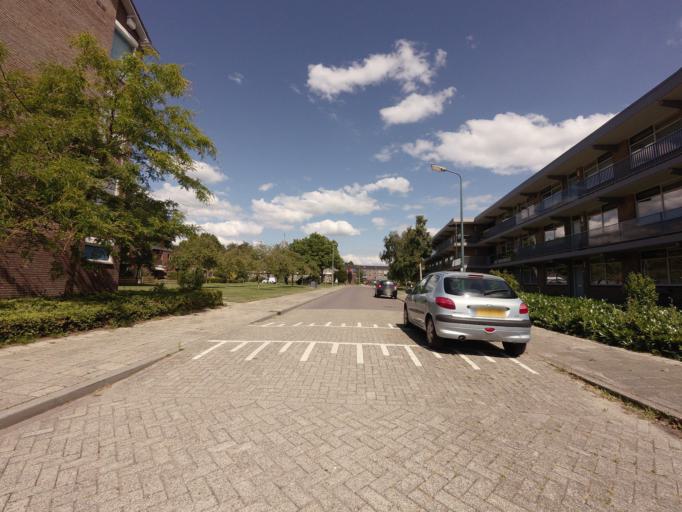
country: NL
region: Utrecht
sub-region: Gemeente Woerden
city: Woerden
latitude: 52.0870
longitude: 4.8700
